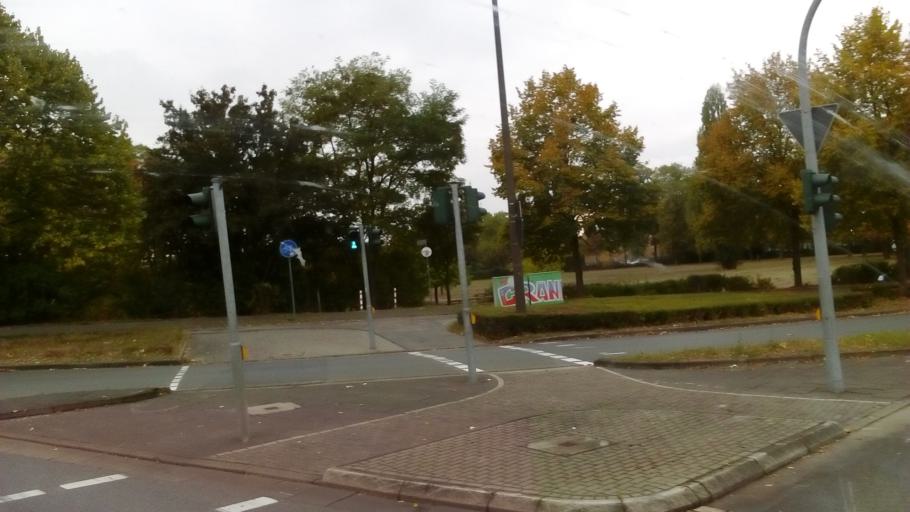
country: DE
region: North Rhine-Westphalia
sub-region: Regierungsbezirk Dusseldorf
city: Hochfeld
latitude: 51.3982
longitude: 6.7108
